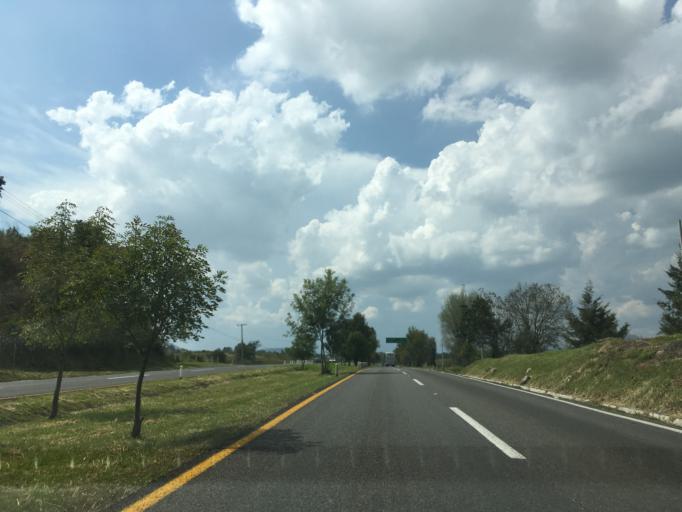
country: MX
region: Michoacan
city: Lagunillas
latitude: 19.5589
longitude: -101.3998
